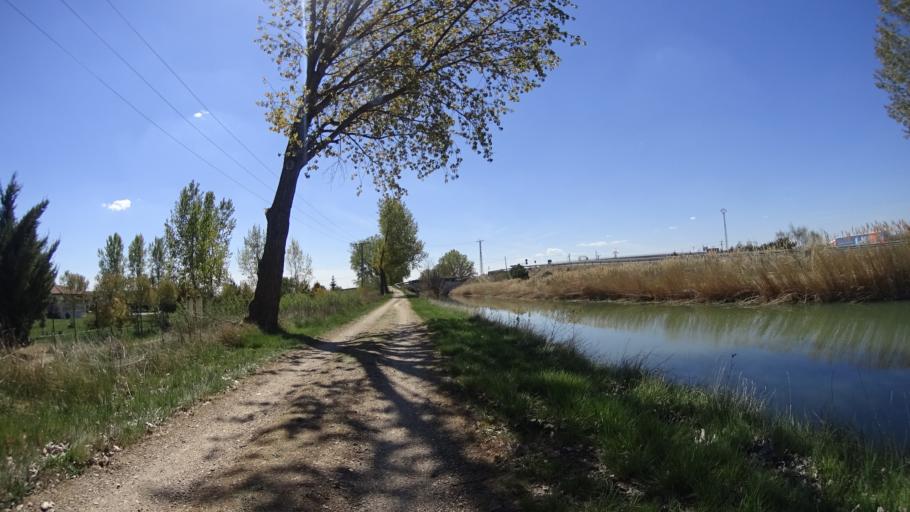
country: ES
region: Castille and Leon
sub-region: Provincia de Valladolid
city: Cabezon
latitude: 41.7426
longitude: -4.6598
